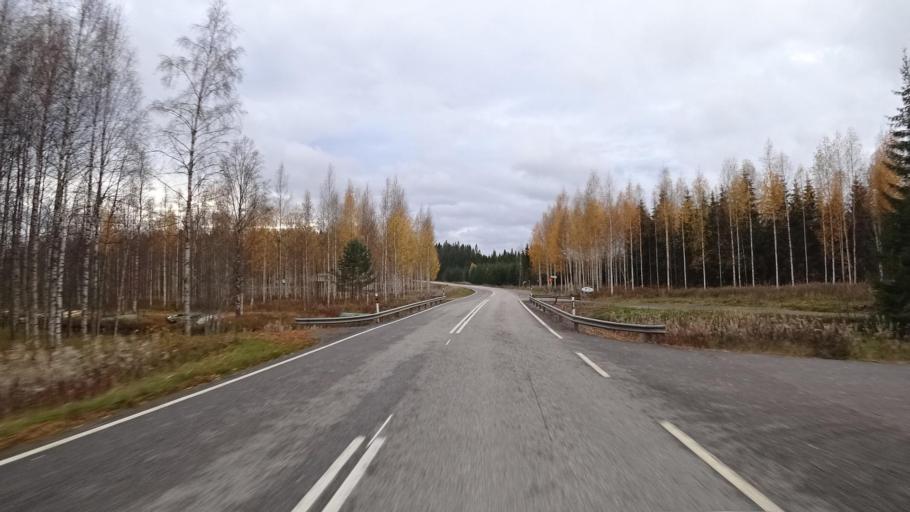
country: FI
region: Central Finland
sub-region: Joutsa
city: Leivonmaeki
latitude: 61.8450
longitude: 26.2345
